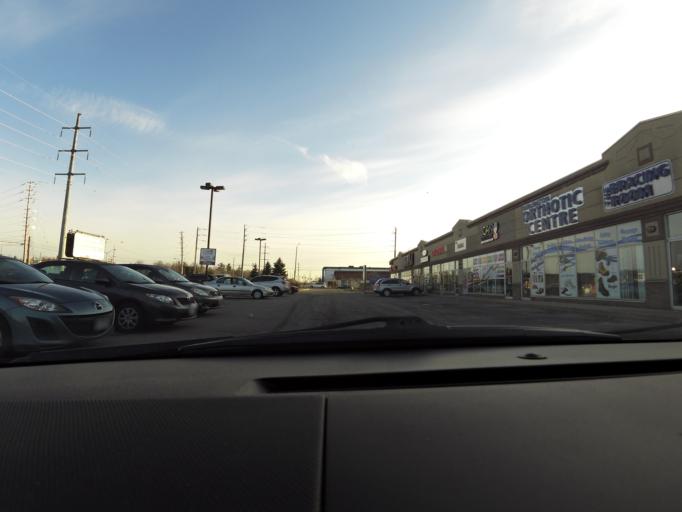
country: CA
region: Ontario
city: Burlington
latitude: 43.3781
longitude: -79.8062
